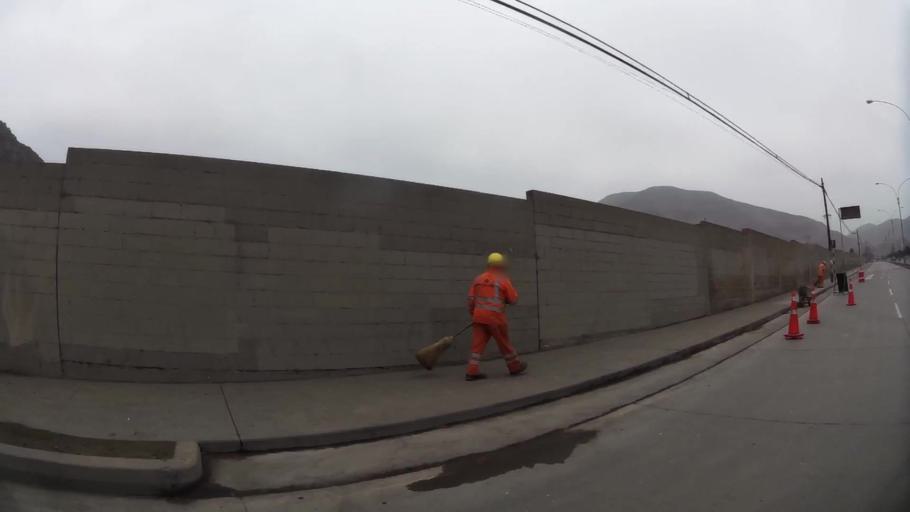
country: PE
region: Lima
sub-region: Lima
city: Cieneguilla
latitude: -12.2035
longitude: -76.9076
